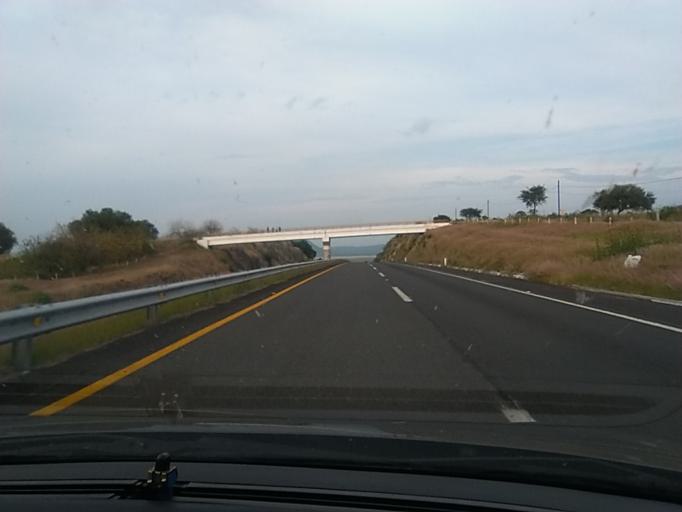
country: MX
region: Michoacan
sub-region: Zinapecuaro
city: Francisco Villa
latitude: 19.8907
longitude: -100.9071
